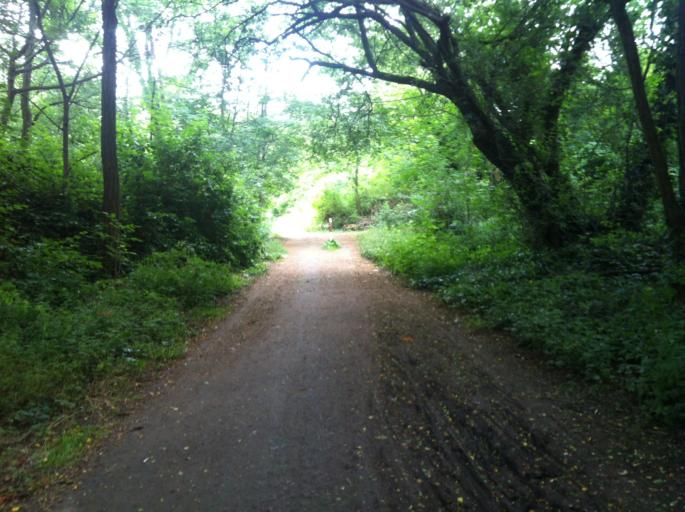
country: DE
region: Rheinland-Pfalz
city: Mainz
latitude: 50.0018
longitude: 8.2426
